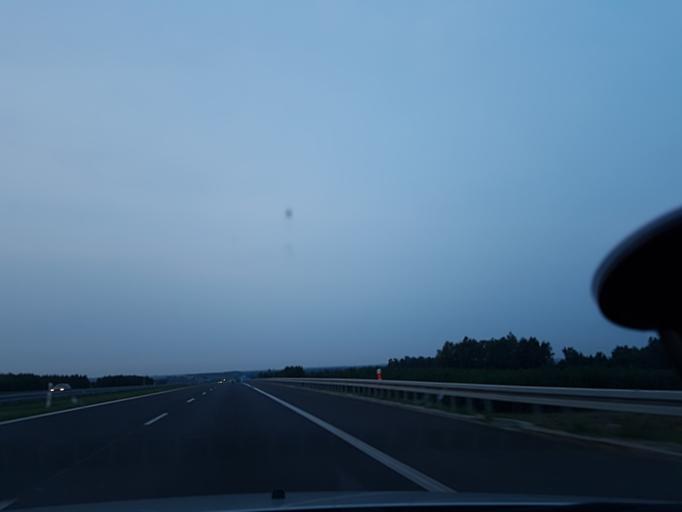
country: PL
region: Lodz Voivodeship
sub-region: Powiat zgierski
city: Strykow
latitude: 51.9207
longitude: 19.6191
